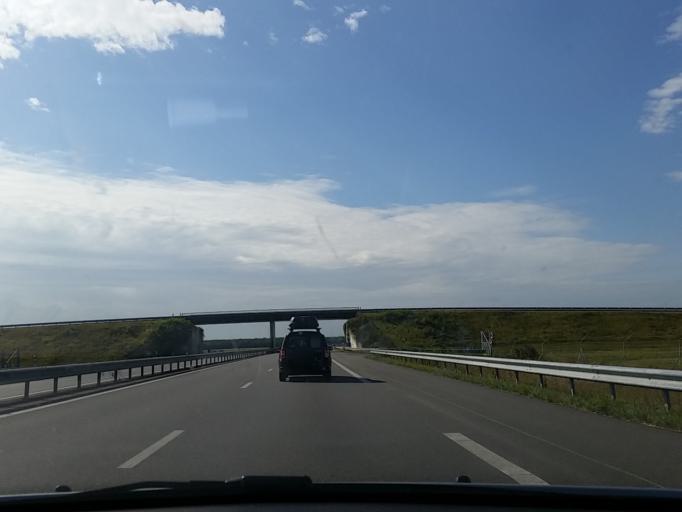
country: FR
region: Centre
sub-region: Departement du Cher
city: Levet
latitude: 46.8644
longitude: 2.4274
